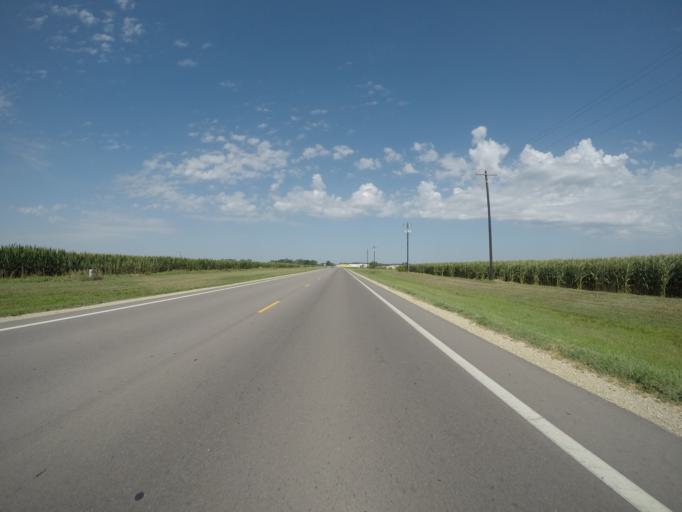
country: US
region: Kansas
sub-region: Clay County
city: Clay Center
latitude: 39.3799
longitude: -97.1536
